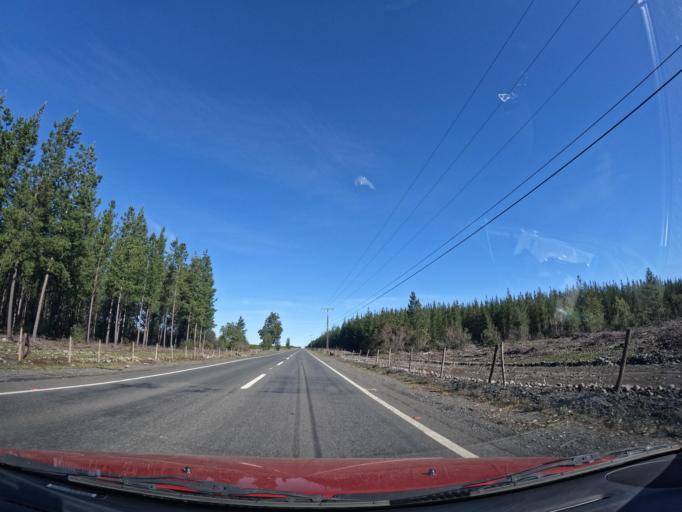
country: CL
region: Biobio
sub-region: Provincia de Biobio
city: Los Angeles
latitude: -37.3104
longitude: -71.9784
